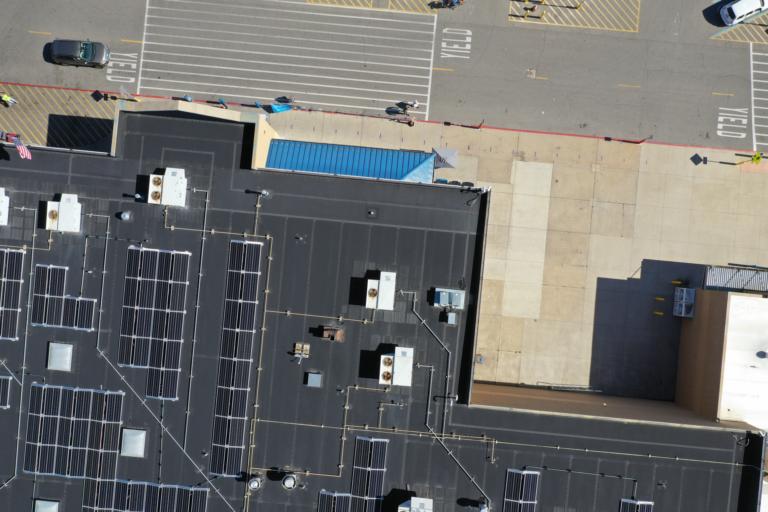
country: US
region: Illinois
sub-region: Tazewell County
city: Pekin
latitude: 40.5384
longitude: -89.5942
